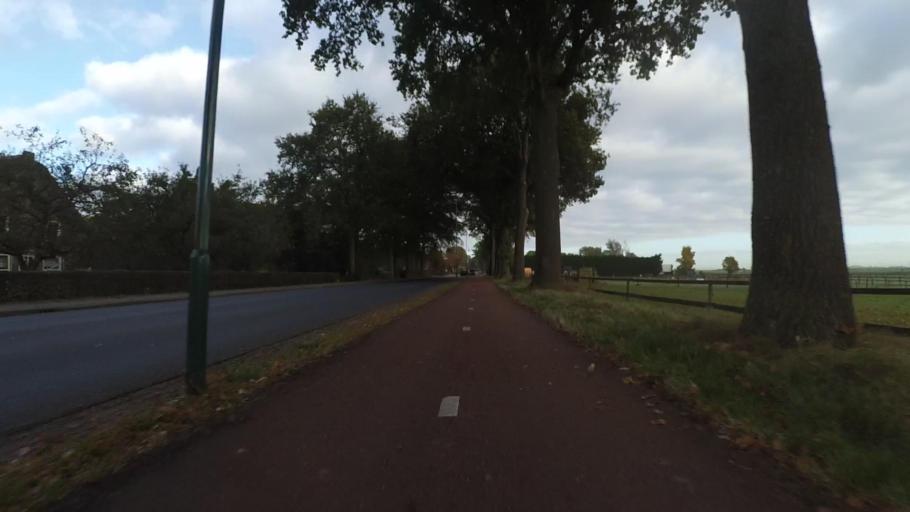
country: NL
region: North Holland
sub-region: Gemeente Blaricum
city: Blaricum
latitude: 52.2489
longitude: 5.2657
